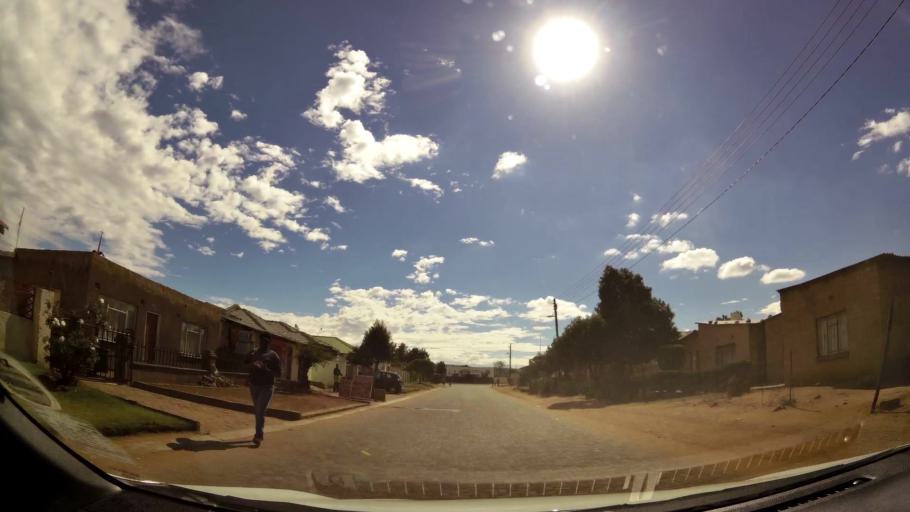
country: ZA
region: Limpopo
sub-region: Waterberg District Municipality
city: Bela-Bela
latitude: -24.8866
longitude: 28.3203
